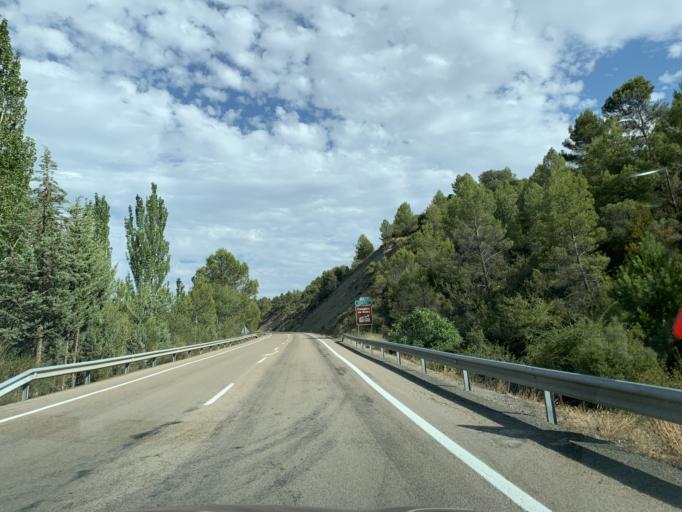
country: ES
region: Aragon
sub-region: Provincia de Zaragoza
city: Santa Eulalia de Gallego
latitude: 42.2944
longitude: -0.7285
